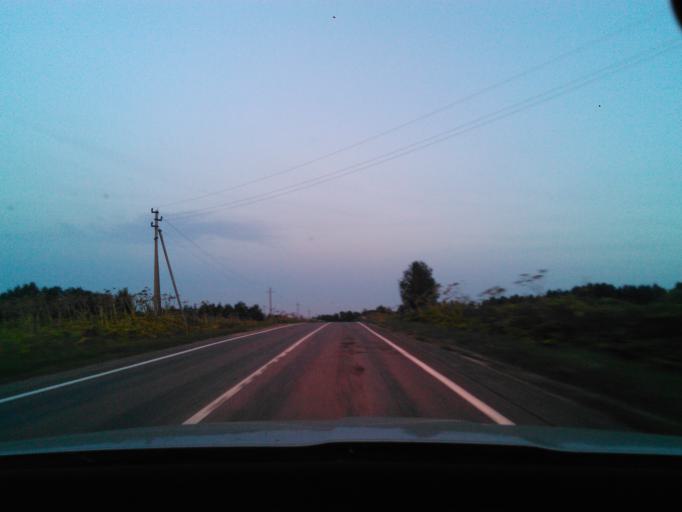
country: RU
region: Moskovskaya
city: Klin
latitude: 56.1615
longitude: 36.7434
